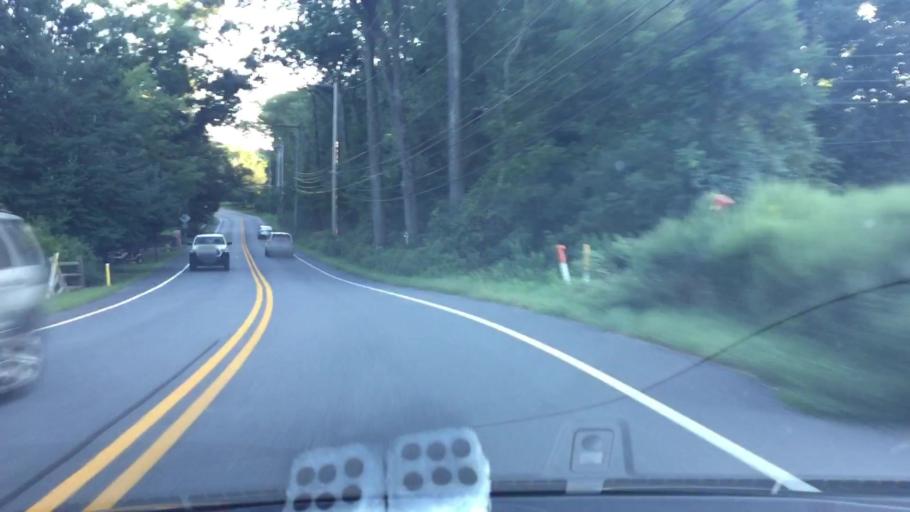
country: US
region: Pennsylvania
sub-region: Delaware County
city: Chester Heights
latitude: 39.8430
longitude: -75.4923
